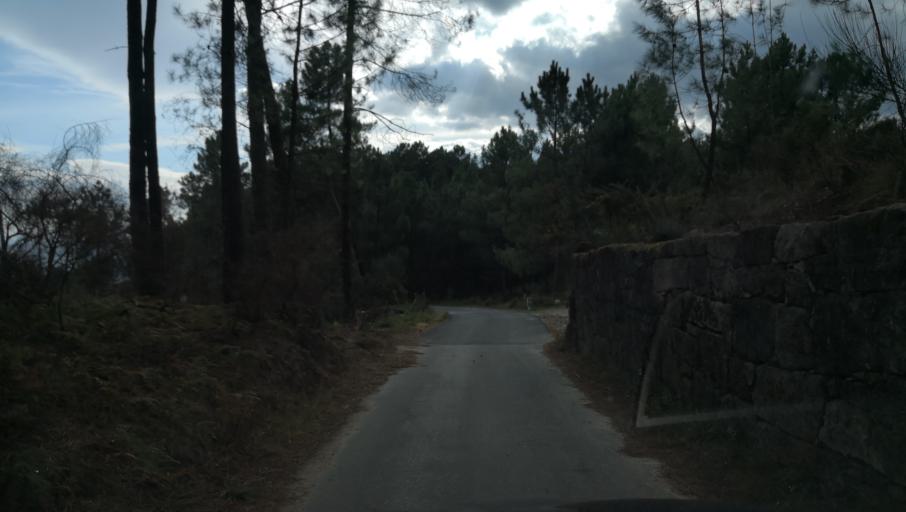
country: PT
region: Vila Real
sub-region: Vila Real
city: Vila Real
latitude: 41.3250
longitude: -7.7755
